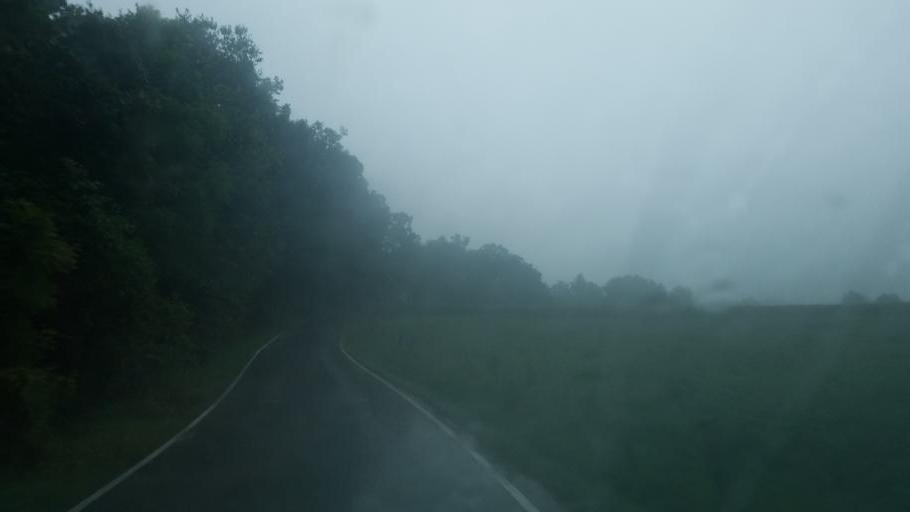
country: US
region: Kentucky
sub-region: Lewis County
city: Vanceburg
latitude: 38.4786
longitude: -83.5117
